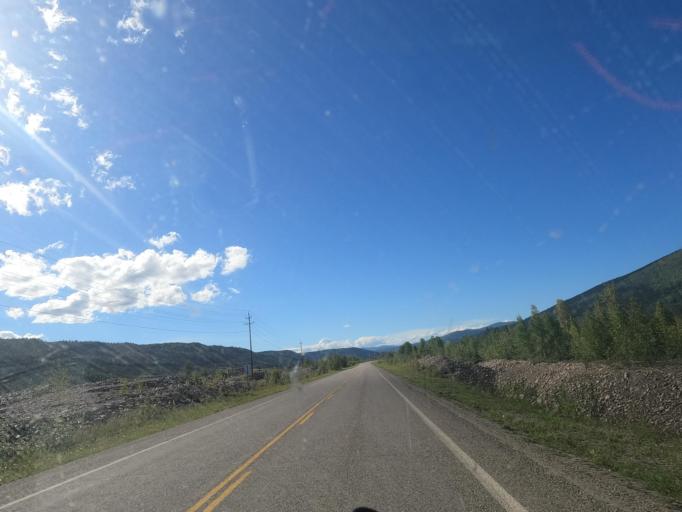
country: CA
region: Yukon
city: Dawson City
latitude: 64.0343
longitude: -139.2748
